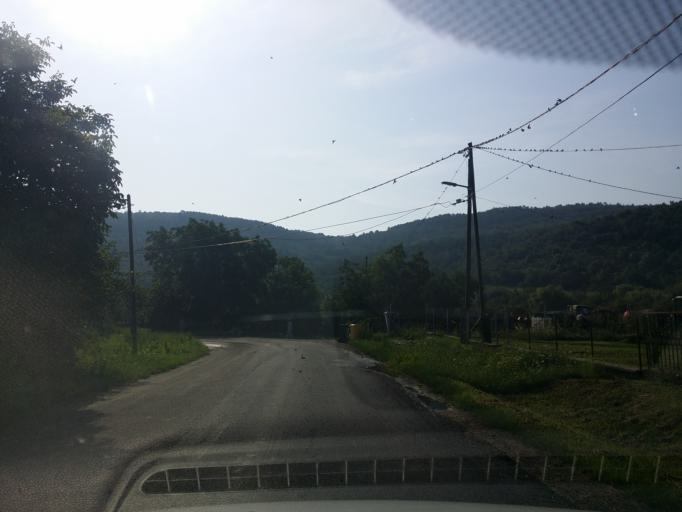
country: HU
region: Borsod-Abauj-Zemplen
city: Gonc
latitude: 48.3887
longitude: 21.2805
